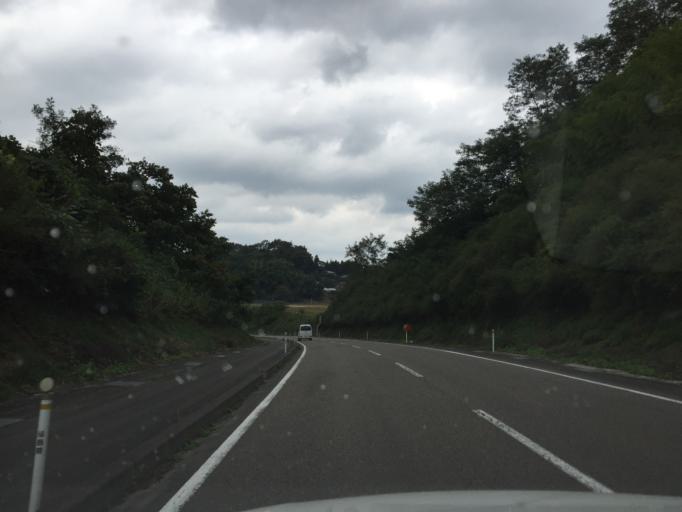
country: JP
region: Fukushima
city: Miharu
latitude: 37.4410
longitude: 140.5106
